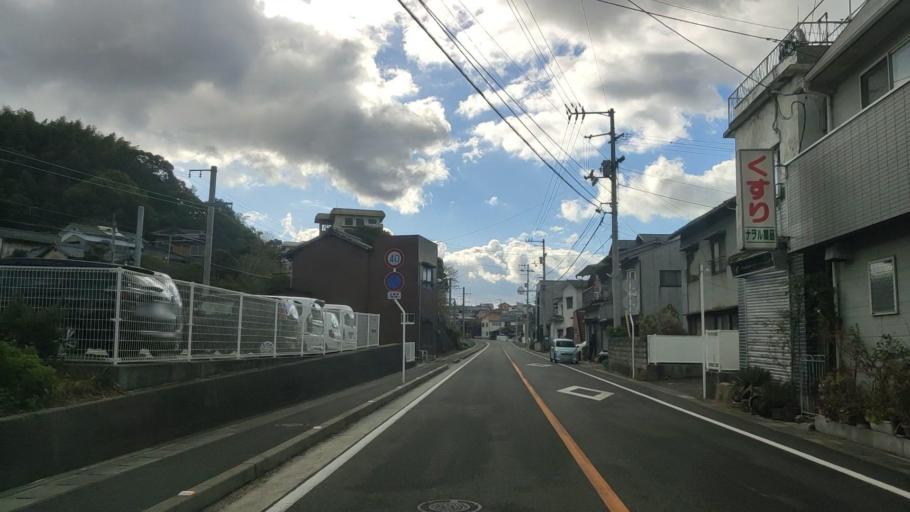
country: JP
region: Ehime
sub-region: Shikoku-chuo Shi
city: Matsuyama
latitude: 33.8824
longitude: 132.7019
